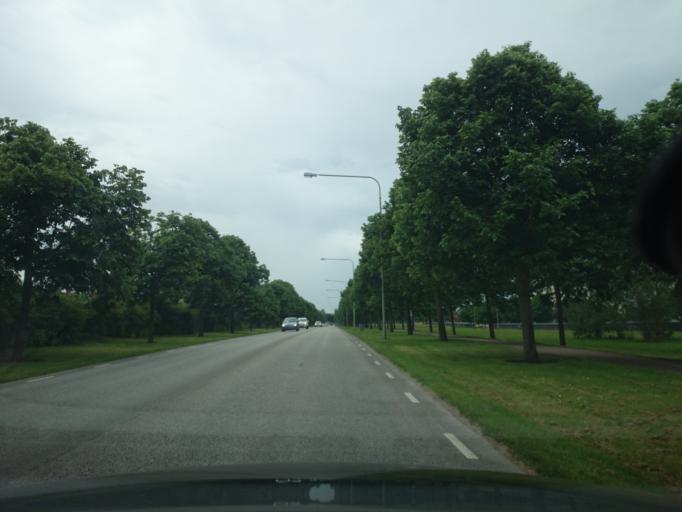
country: SE
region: Skane
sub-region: Landskrona
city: Landskrona
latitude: 55.8921
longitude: 12.8286
